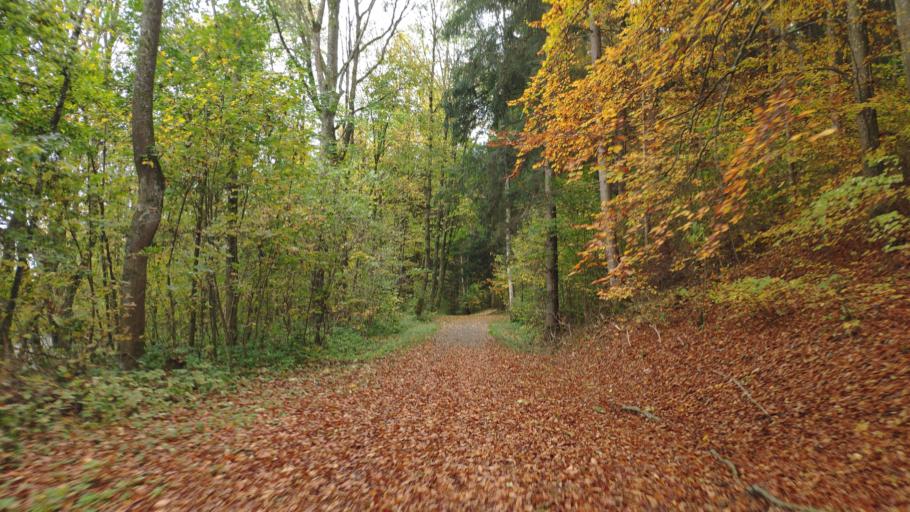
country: DE
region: Baden-Wuerttemberg
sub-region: Tuebingen Region
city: Ulm
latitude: 48.4053
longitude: 9.9305
